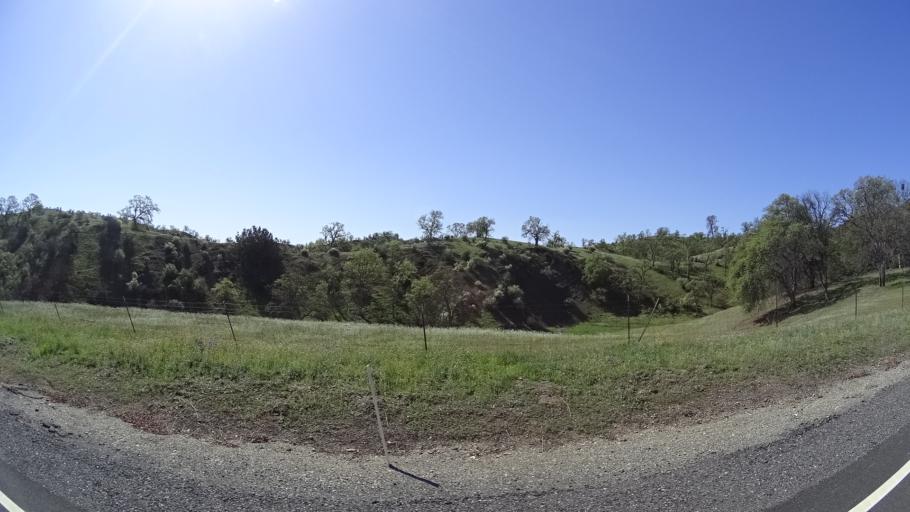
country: US
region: California
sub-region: Glenn County
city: Orland
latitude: 39.6541
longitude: -122.5858
